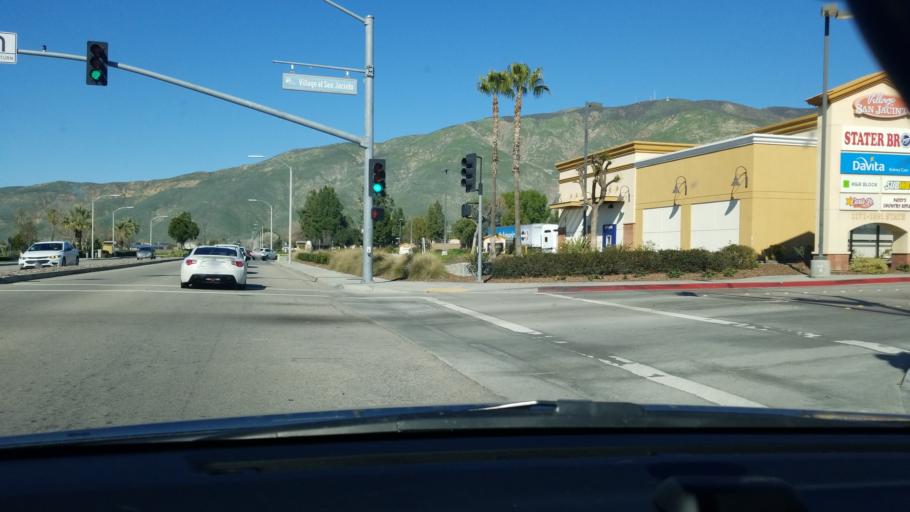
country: US
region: California
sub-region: Riverside County
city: San Jacinto
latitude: 33.8037
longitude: -116.9720
